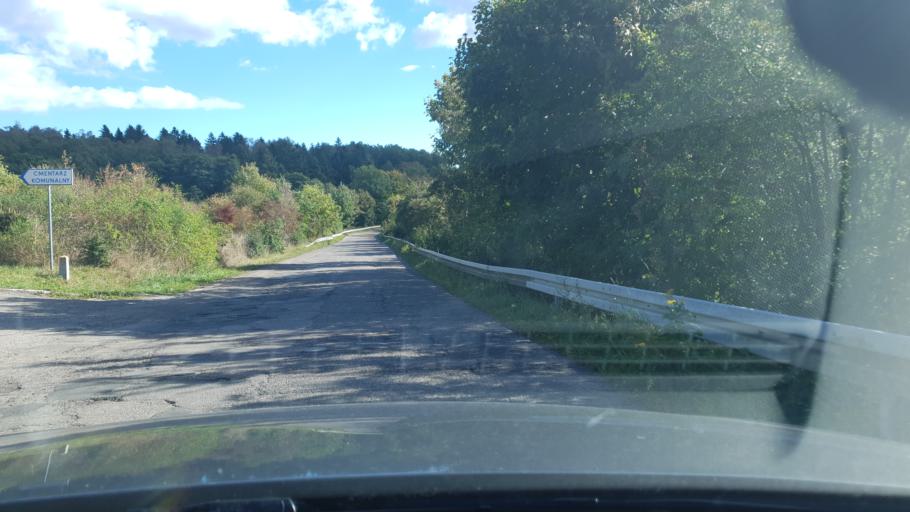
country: PL
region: Pomeranian Voivodeship
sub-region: Powiat pucki
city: Zelistrzewo
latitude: 54.6898
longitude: 18.4227
